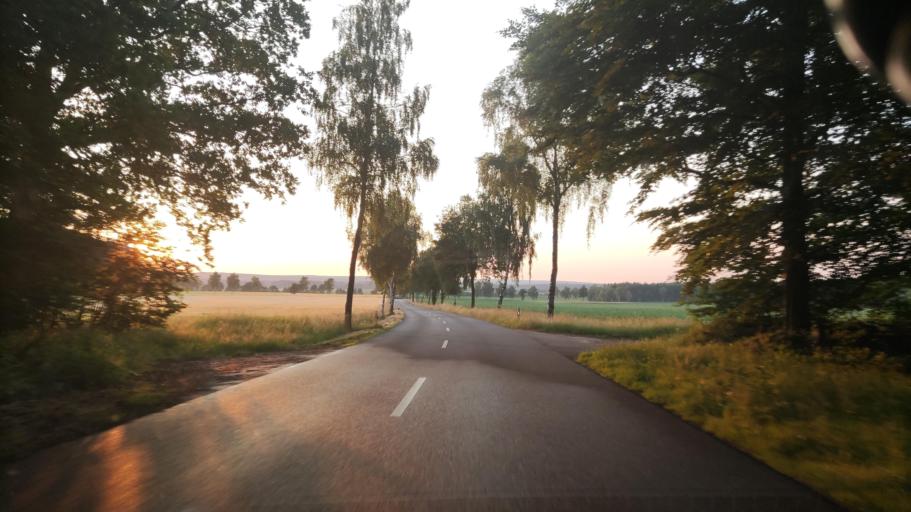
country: DE
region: Lower Saxony
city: Bispingen
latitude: 53.1255
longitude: 10.0505
